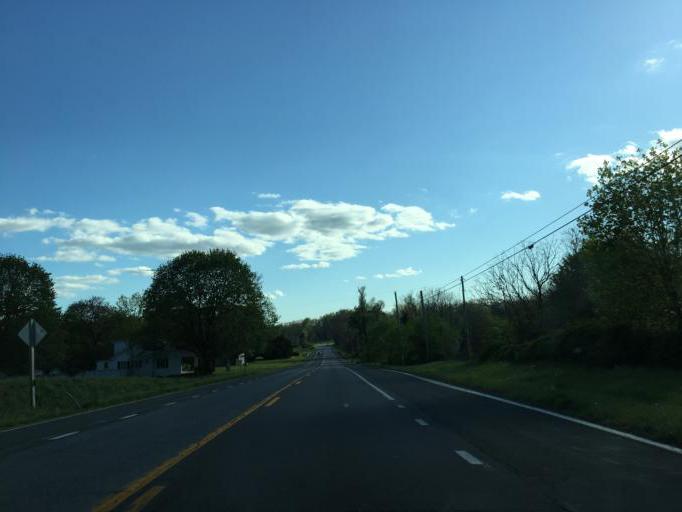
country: US
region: Maryland
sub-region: Frederick County
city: Woodsboro
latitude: 39.5519
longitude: -77.3076
